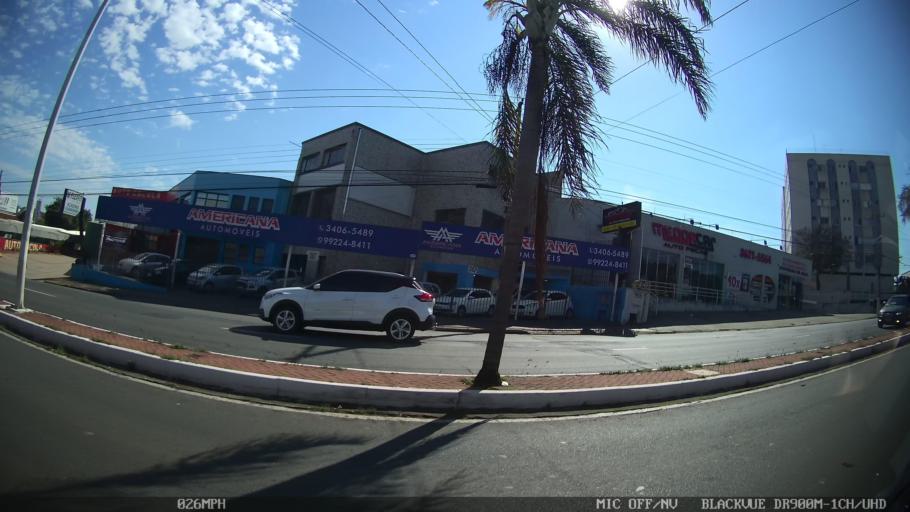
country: BR
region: Sao Paulo
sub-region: Americana
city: Americana
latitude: -22.7331
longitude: -47.3247
